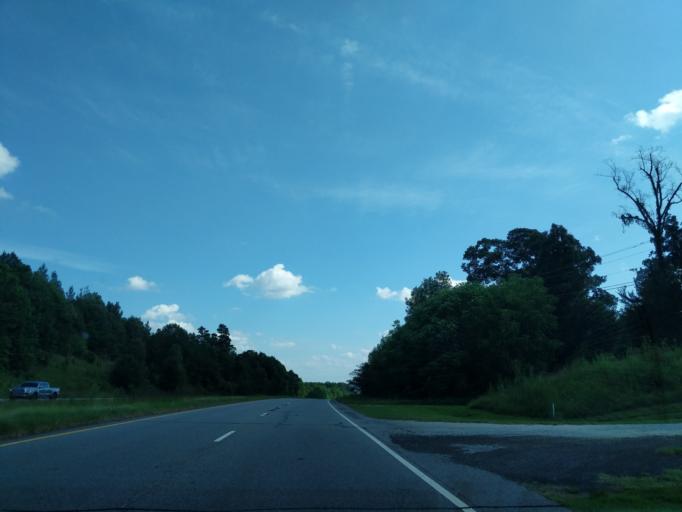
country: US
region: Georgia
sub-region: Banks County
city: Homer
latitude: 34.2852
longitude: -83.4672
